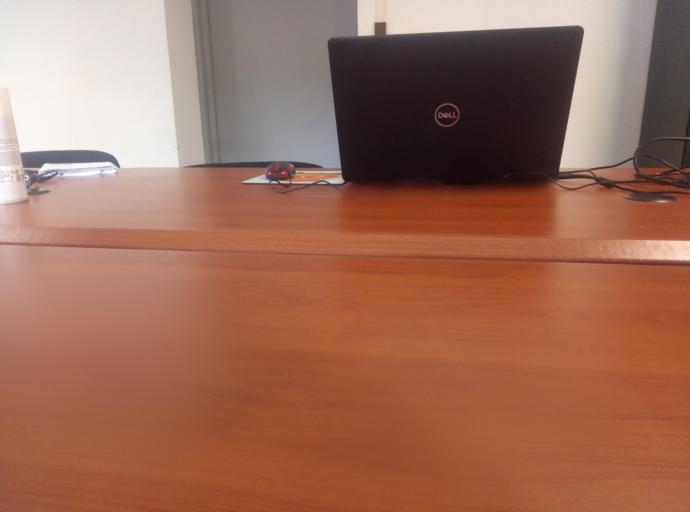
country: MG
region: Analamanga
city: Antananarivo
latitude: -18.8725
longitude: 47.5259
